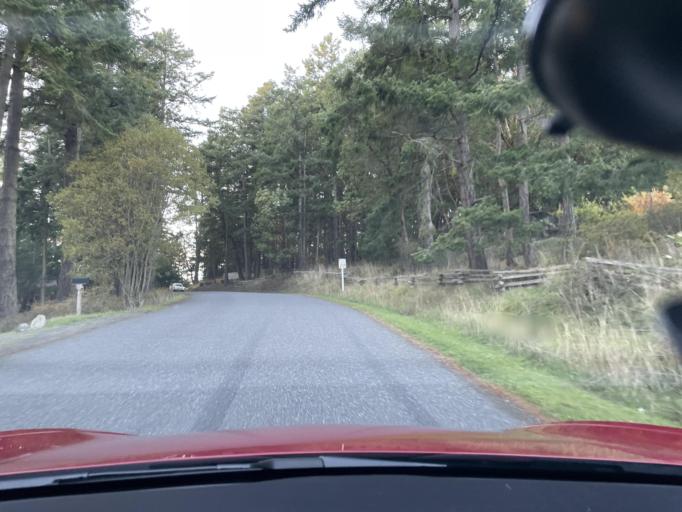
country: US
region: Washington
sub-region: San Juan County
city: Friday Harbor
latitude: 48.6117
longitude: -123.1485
